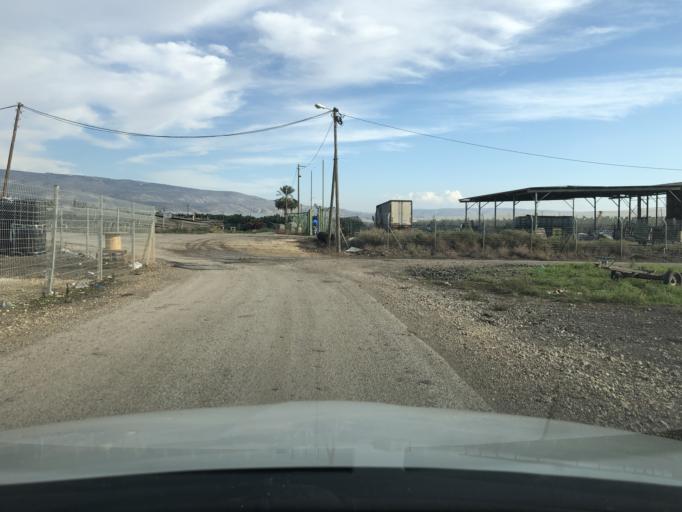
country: IL
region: Northern District
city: Yavne'el
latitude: 32.6559
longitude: 35.5820
